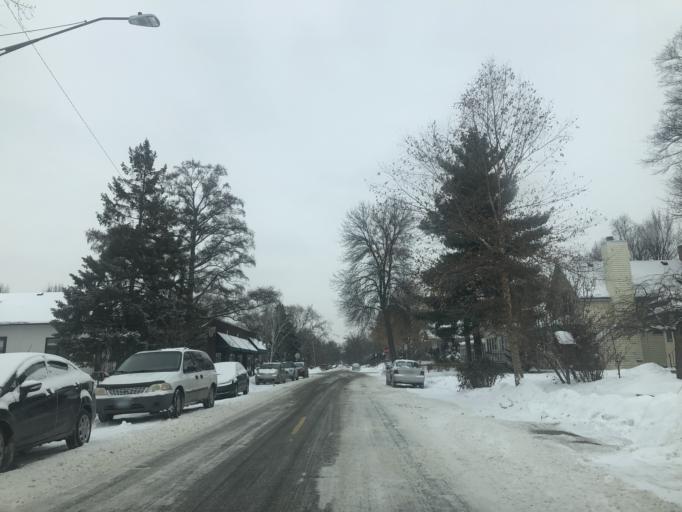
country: US
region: Minnesota
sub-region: Hennepin County
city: Richfield
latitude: 44.9276
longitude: -93.2844
